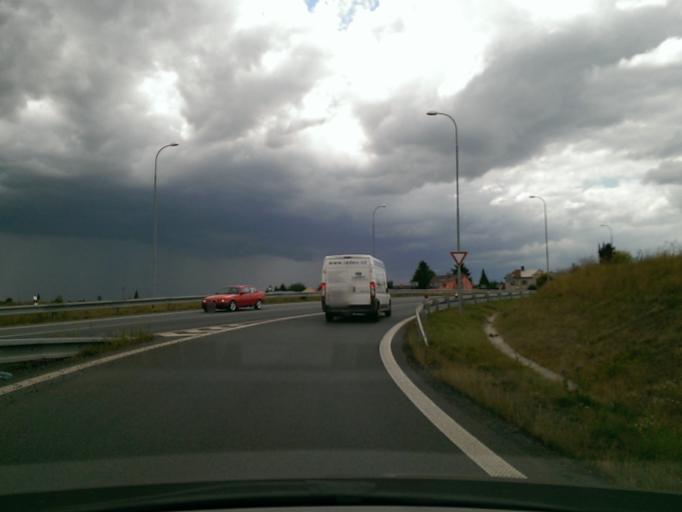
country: CZ
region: Central Bohemia
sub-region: Okres Nymburk
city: Nymburk
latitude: 50.2051
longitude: 15.0363
